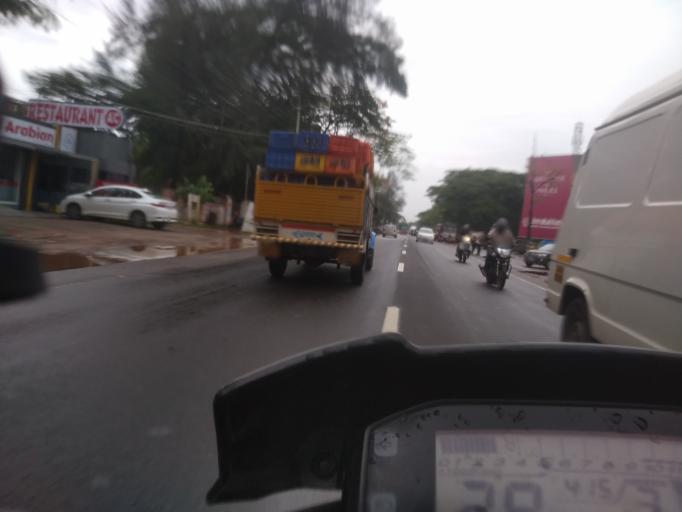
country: IN
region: Kerala
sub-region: Alappuzha
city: Shertallai
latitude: 9.6697
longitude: 76.3395
